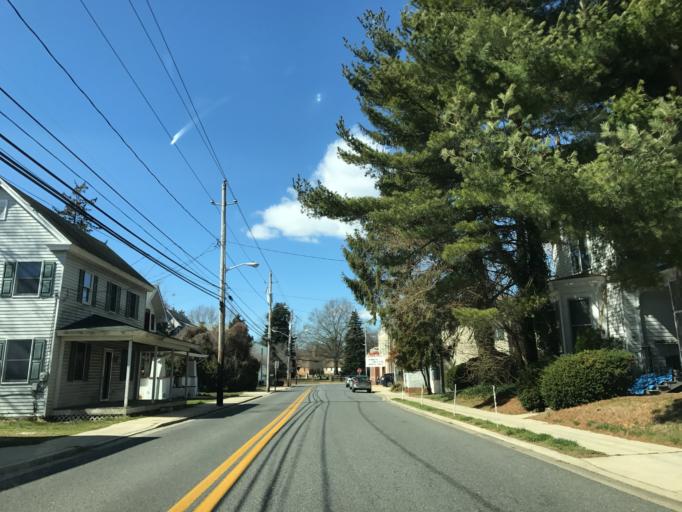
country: US
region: Maryland
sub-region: Queen Anne's County
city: Kingstown
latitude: 39.1414
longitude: -75.9843
